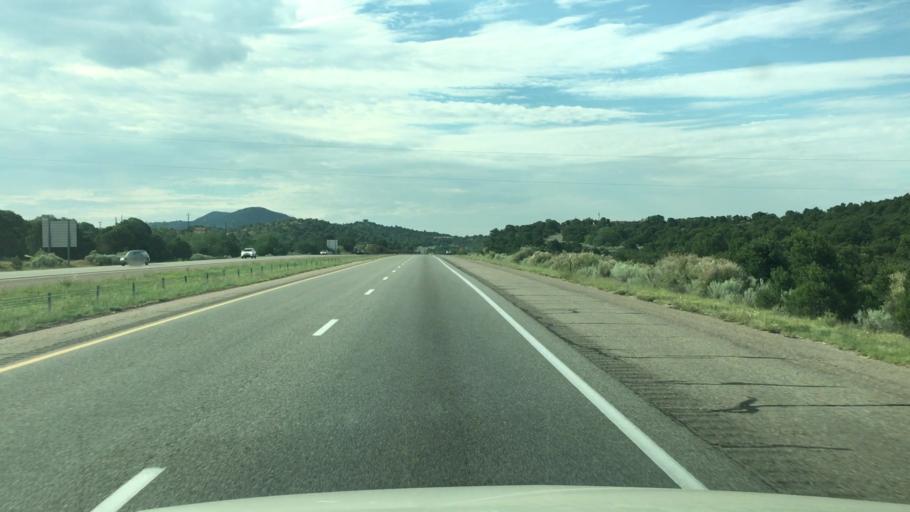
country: US
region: New Mexico
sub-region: Santa Fe County
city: Santa Fe
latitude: 35.6274
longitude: -105.9226
